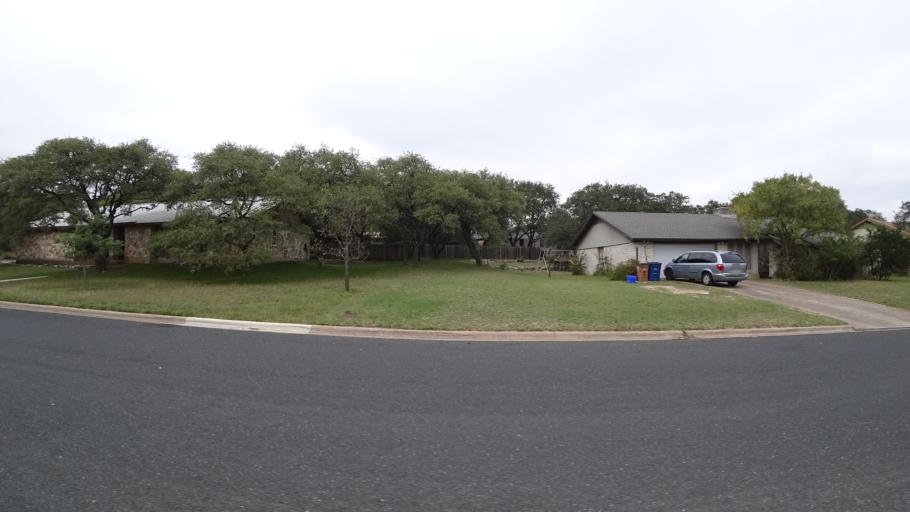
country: US
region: Texas
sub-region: Travis County
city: Barton Creek
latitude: 30.2385
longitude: -97.8898
